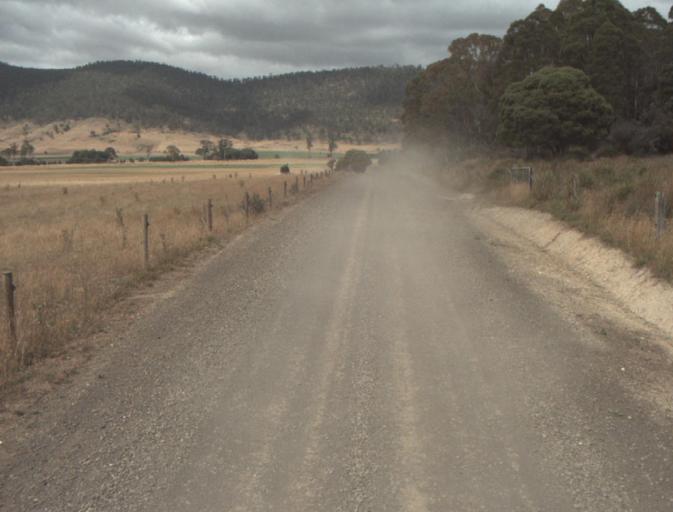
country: AU
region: Tasmania
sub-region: Northern Midlands
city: Evandale
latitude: -41.4738
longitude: 147.4459
